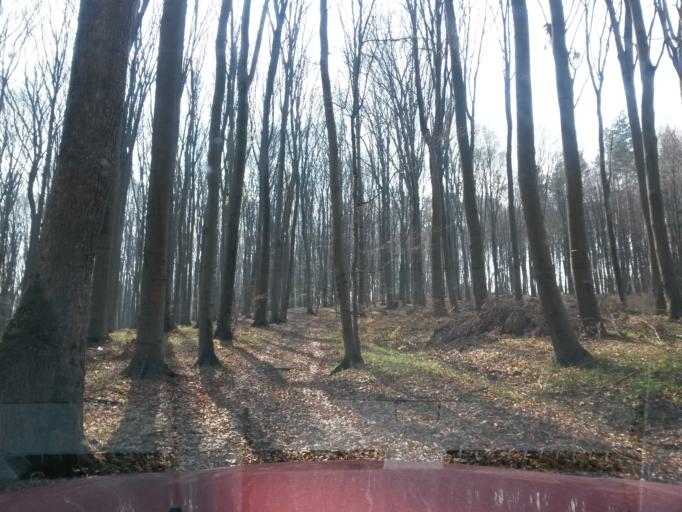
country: SK
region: Presovsky
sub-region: Okres Presov
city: Presov
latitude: 48.9330
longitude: 21.1522
